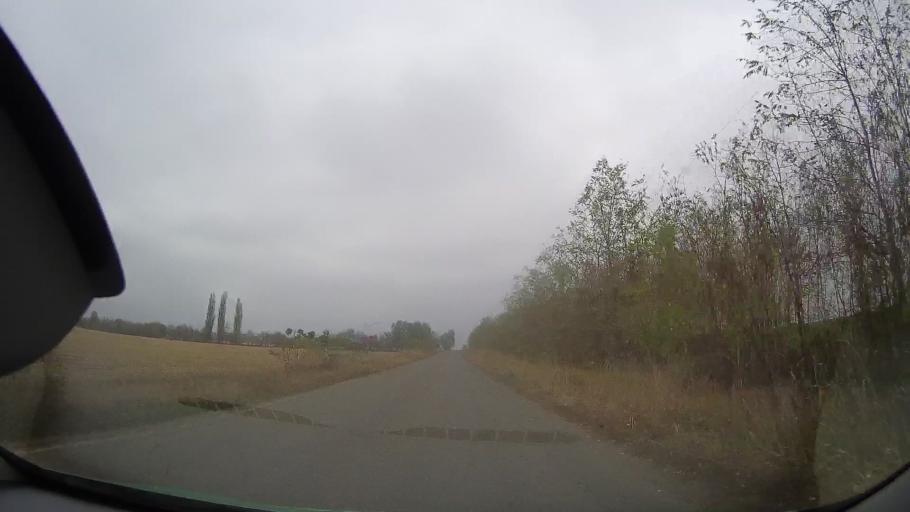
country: RO
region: Buzau
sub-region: Comuna Glodeanu-Silistea
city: Glodeanu-Silistea
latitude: 44.8119
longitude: 26.8526
